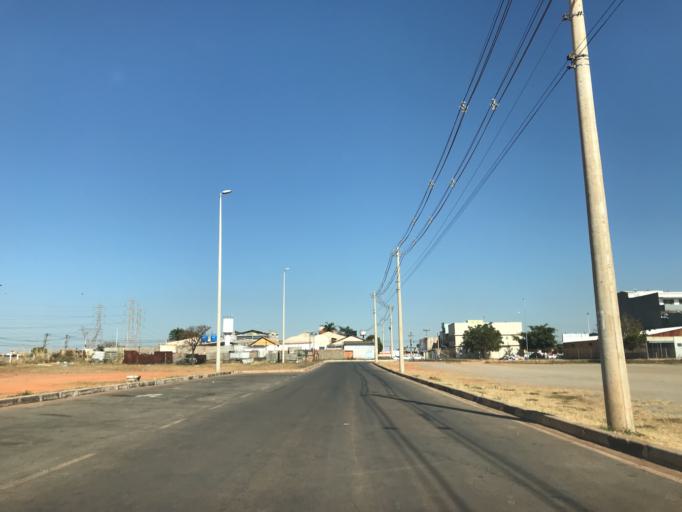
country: BR
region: Federal District
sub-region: Brasilia
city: Brasilia
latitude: -15.8499
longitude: -48.0392
